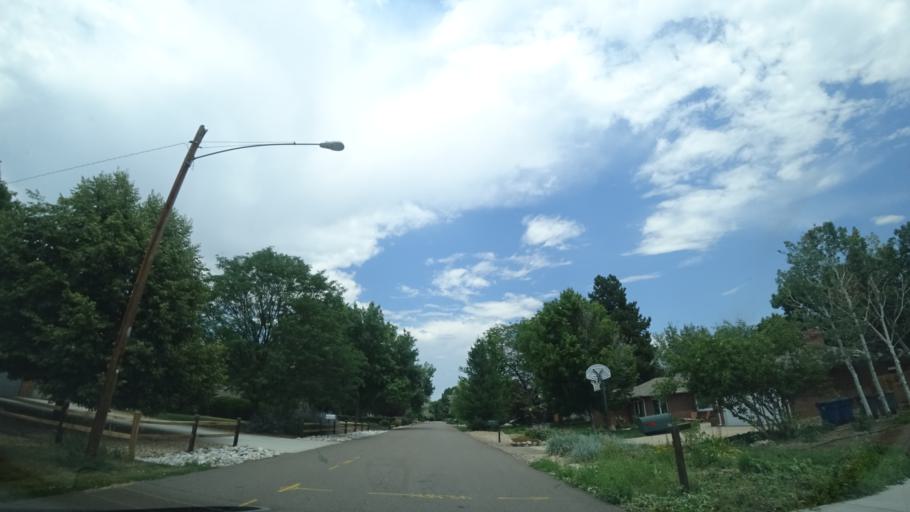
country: US
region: Colorado
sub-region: Jefferson County
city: Lakewood
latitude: 39.7196
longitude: -105.0870
